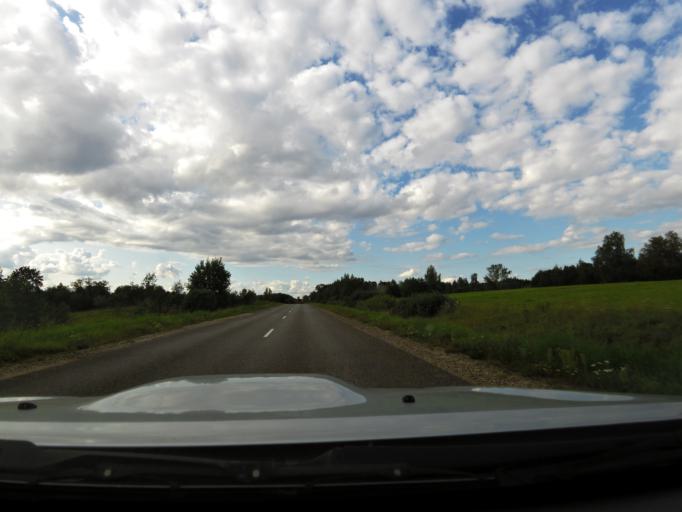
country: LV
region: Akniste
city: Akniste
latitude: 56.0202
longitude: 25.9223
